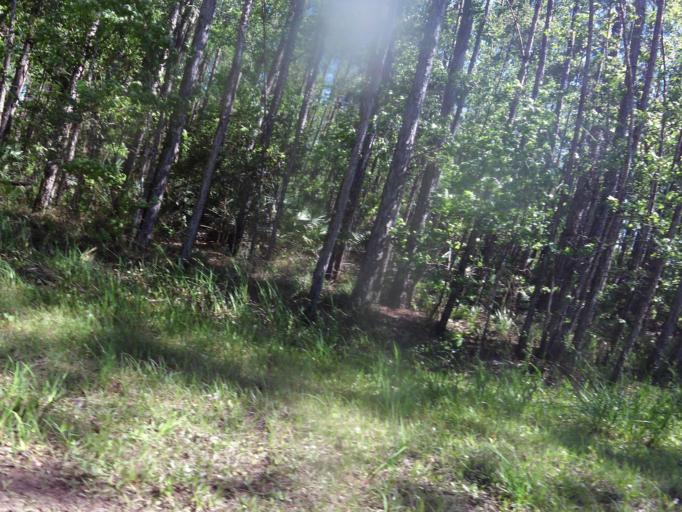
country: US
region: Florida
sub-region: Clay County
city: Green Cove Springs
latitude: 29.9563
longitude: -81.6202
